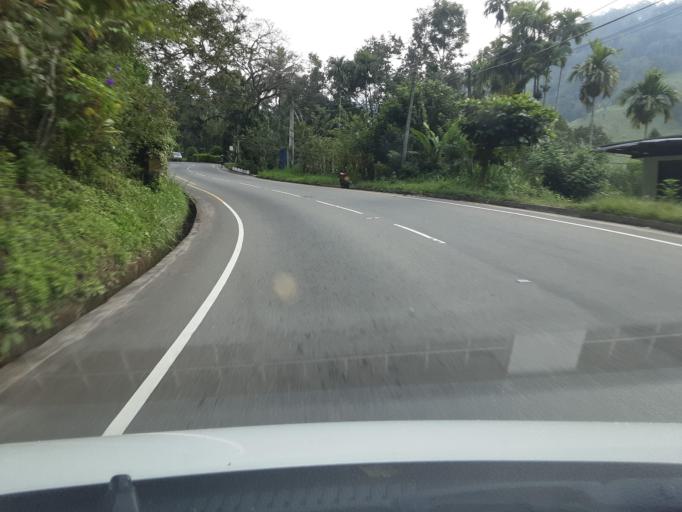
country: LK
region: Uva
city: Badulla
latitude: 6.9426
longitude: 81.0167
